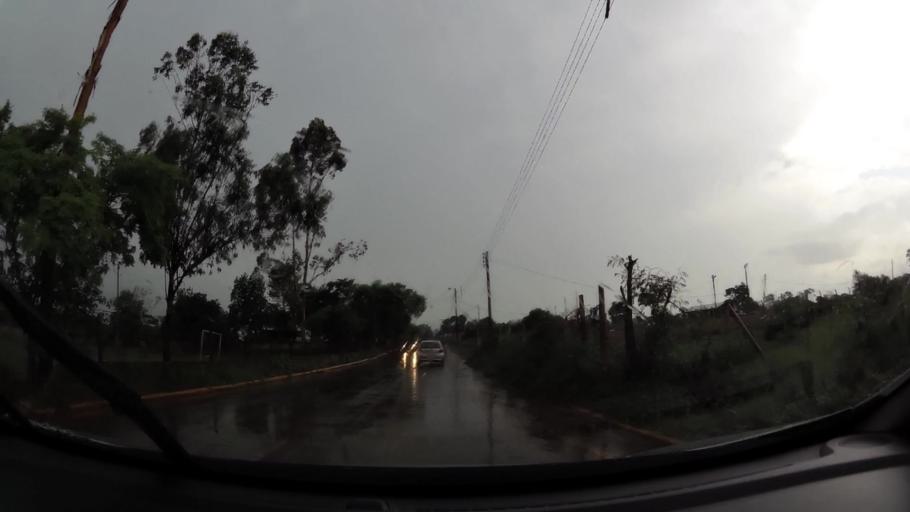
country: PY
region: Alto Parana
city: Presidente Franco
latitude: -25.5369
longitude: -54.6779
